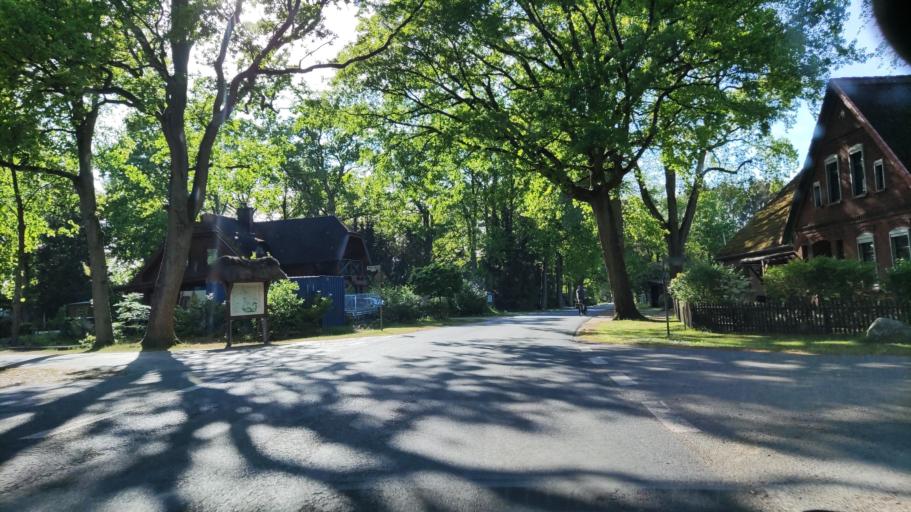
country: DE
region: Lower Saxony
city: Otter
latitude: 53.1837
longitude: 9.7538
